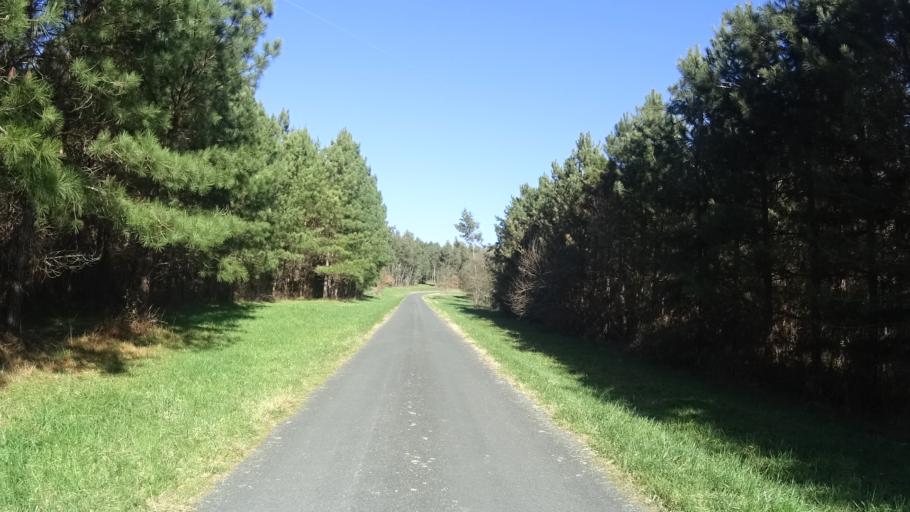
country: FR
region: Aquitaine
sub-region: Departement de la Dordogne
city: Saint-Aulaye
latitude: 45.1226
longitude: 0.2142
